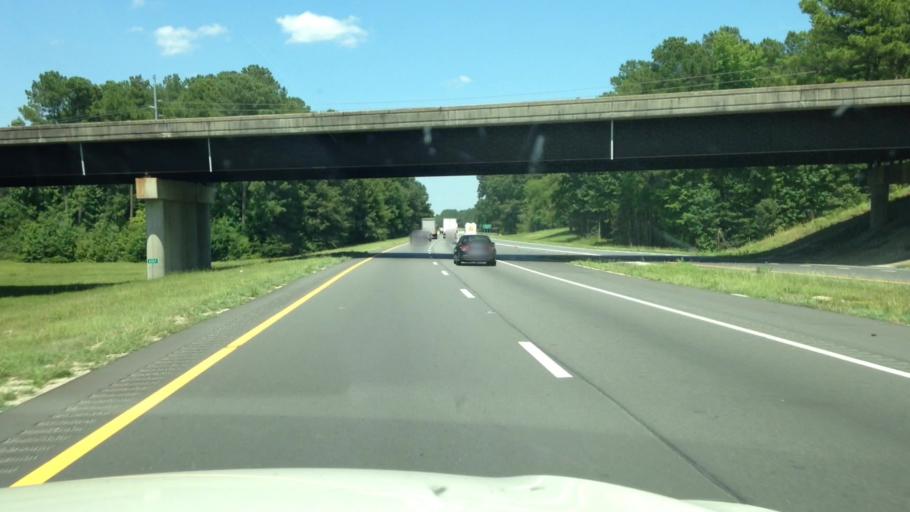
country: US
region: North Carolina
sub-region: Cumberland County
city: Vander
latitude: 34.9797
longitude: -78.8517
